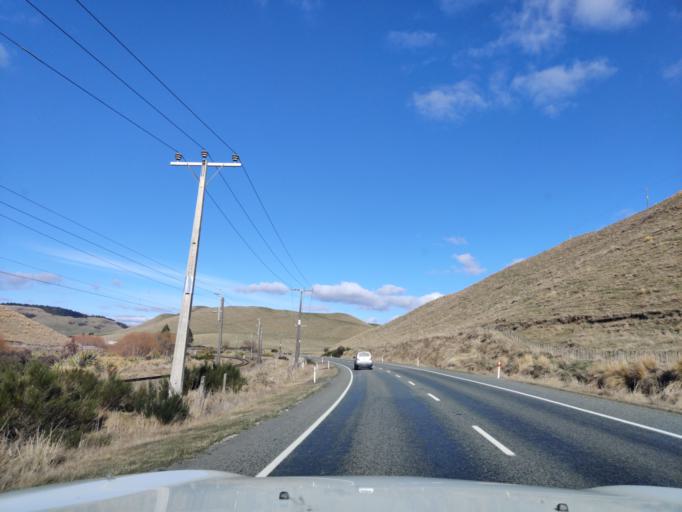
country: NZ
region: Manawatu-Wanganui
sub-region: Ruapehu District
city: Waiouru
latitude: -39.5038
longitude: 175.6740
